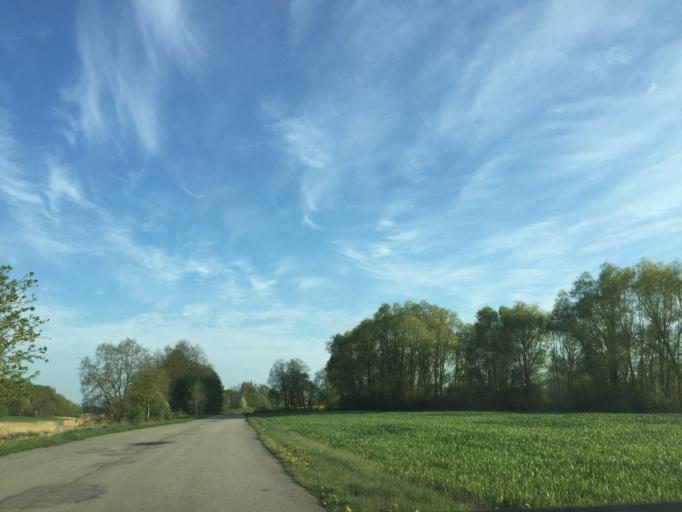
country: LV
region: Bauskas Rajons
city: Bauska
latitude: 56.3189
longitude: 24.2740
